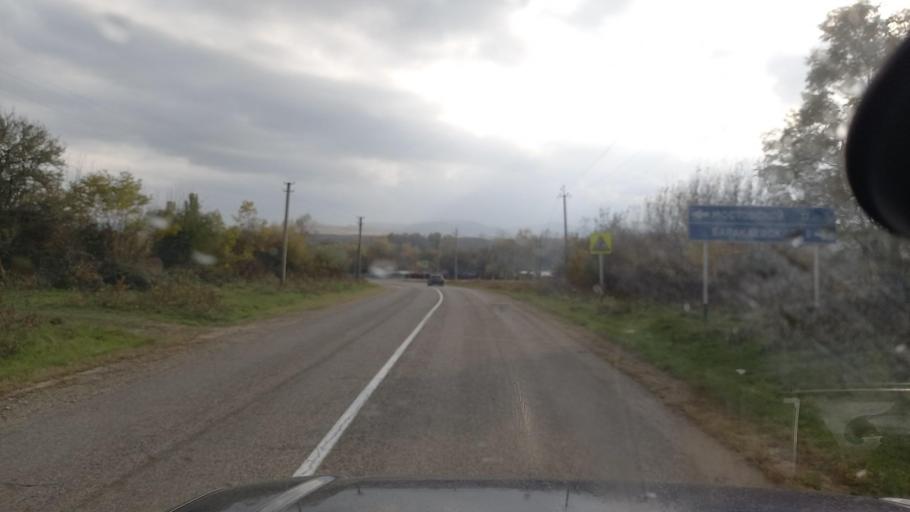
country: RU
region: Krasnodarskiy
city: Gubskaya
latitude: 44.3208
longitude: 40.6069
